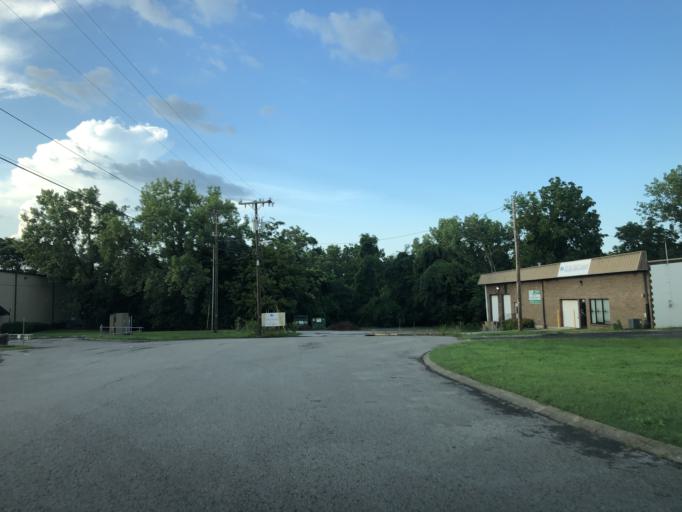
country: US
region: Tennessee
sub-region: Davidson County
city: Nashville
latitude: 36.1458
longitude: -86.7379
